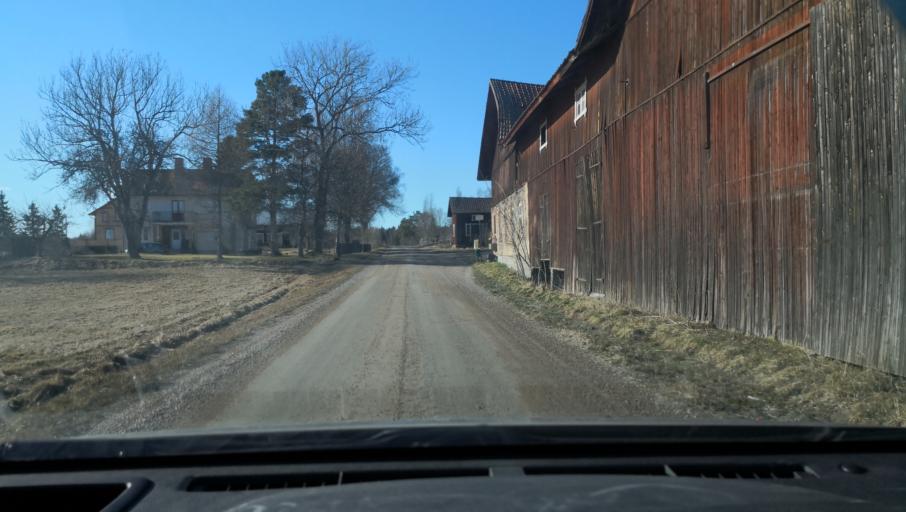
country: SE
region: Vaestmanland
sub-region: Sala Kommun
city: Sala
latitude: 60.1523
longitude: 16.6360
